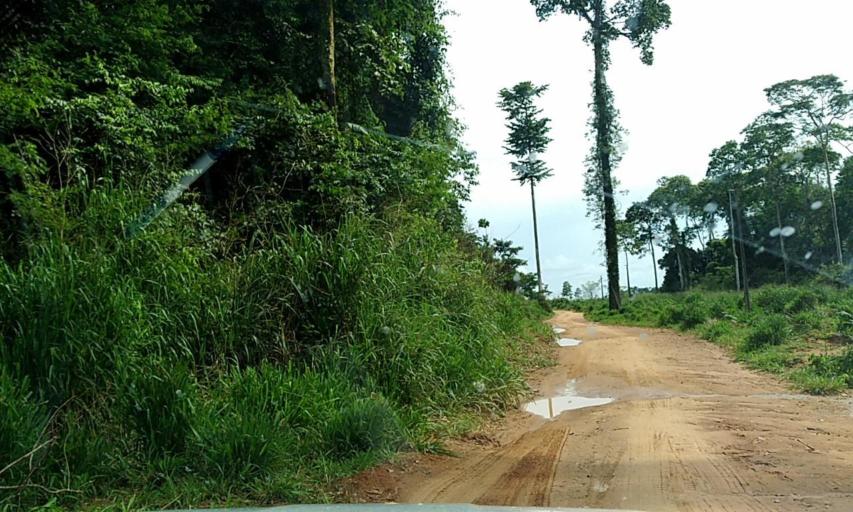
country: BR
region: Para
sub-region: Altamira
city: Altamira
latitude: -3.2350
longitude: -52.7460
